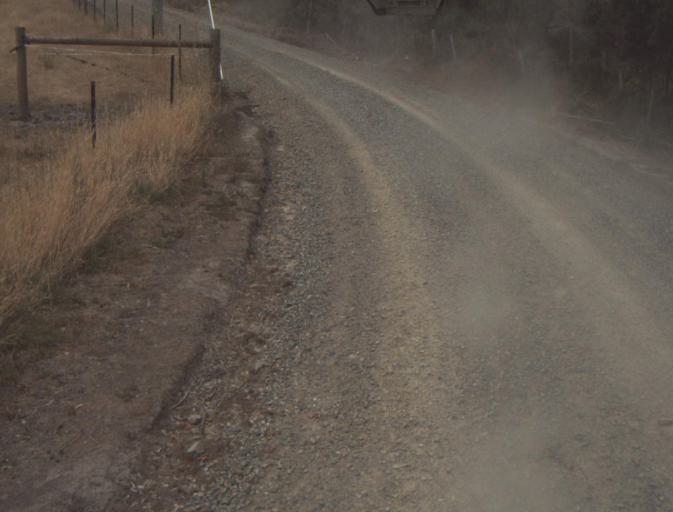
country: AU
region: Tasmania
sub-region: Launceston
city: Mayfield
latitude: -41.2406
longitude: 147.1619
